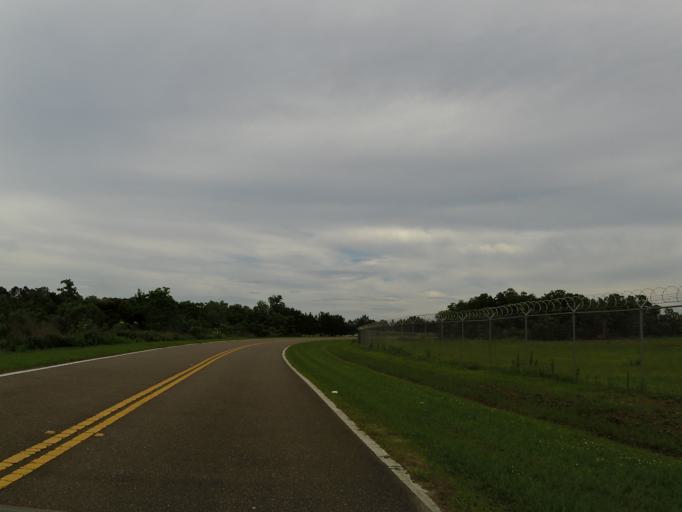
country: US
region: Florida
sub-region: Nassau County
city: Nassau Village-Ratliff
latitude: 30.5468
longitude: -81.7256
